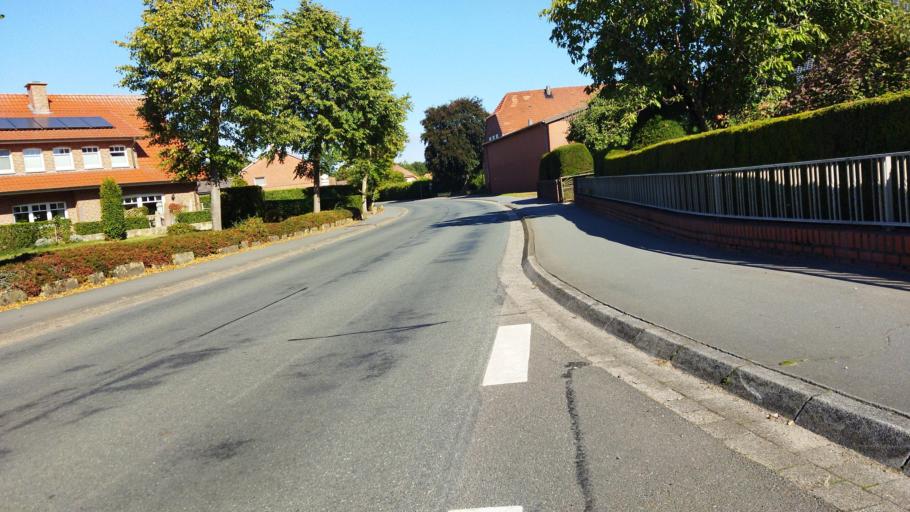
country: DE
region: Lower Saxony
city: Ohne
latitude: 52.2540
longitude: 7.3184
